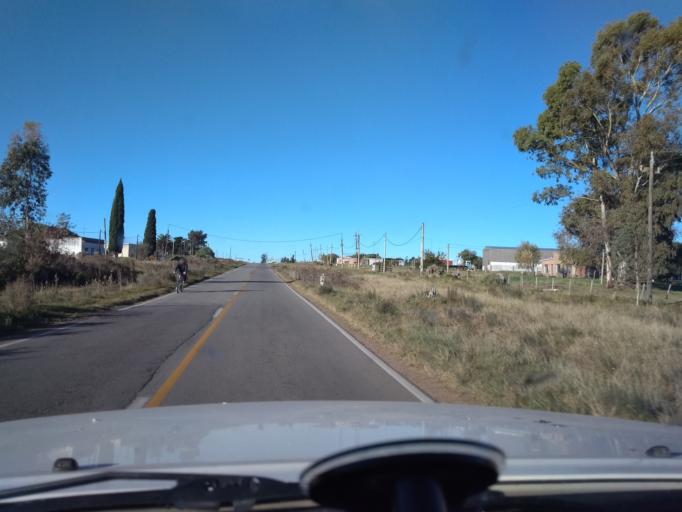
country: UY
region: Canelones
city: Santa Rosa
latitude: -34.4907
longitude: -56.0206
